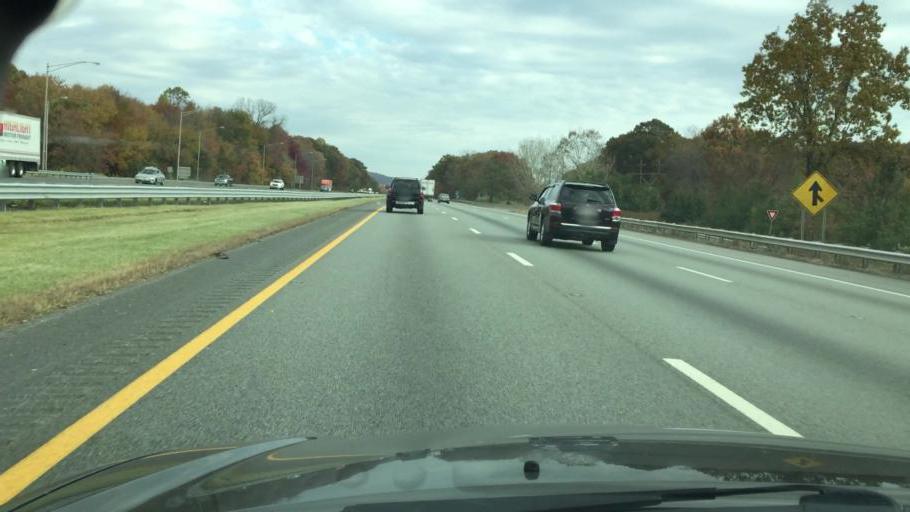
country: US
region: New Jersey
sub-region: Morris County
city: Kenvil
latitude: 40.8979
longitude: -74.6329
